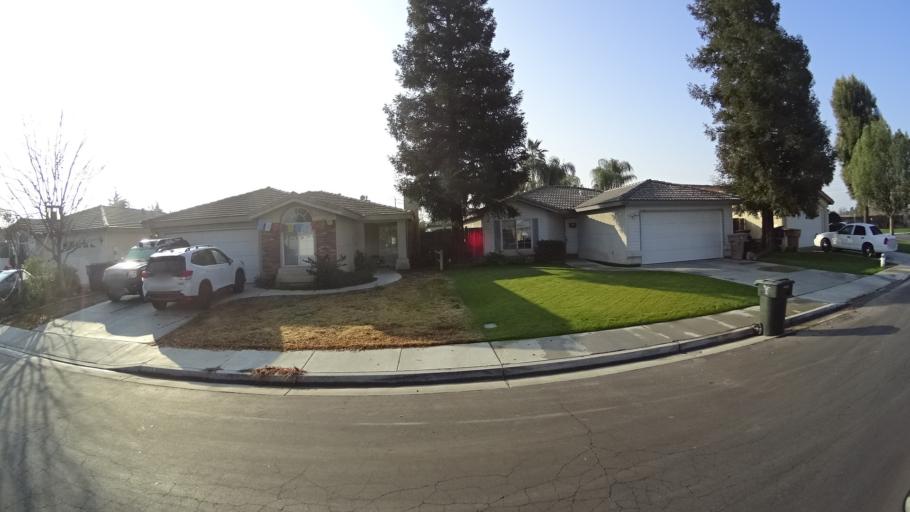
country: US
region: California
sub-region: Kern County
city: Greenacres
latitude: 35.3247
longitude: -119.0944
